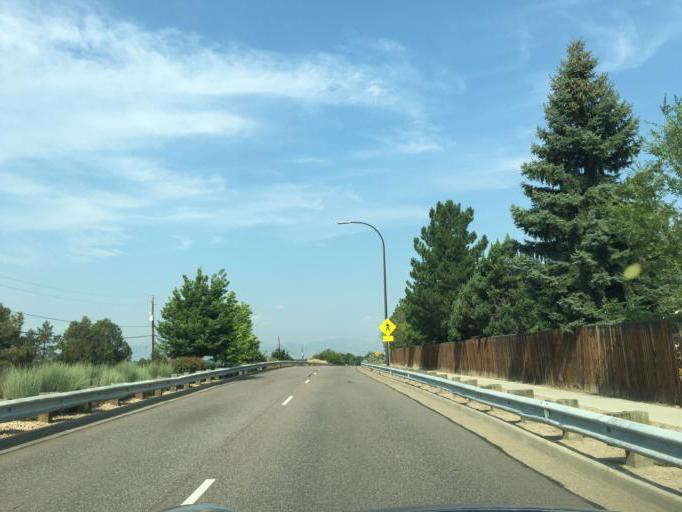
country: US
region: Colorado
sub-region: Adams County
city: Westminster
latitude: 39.8413
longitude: -105.0700
